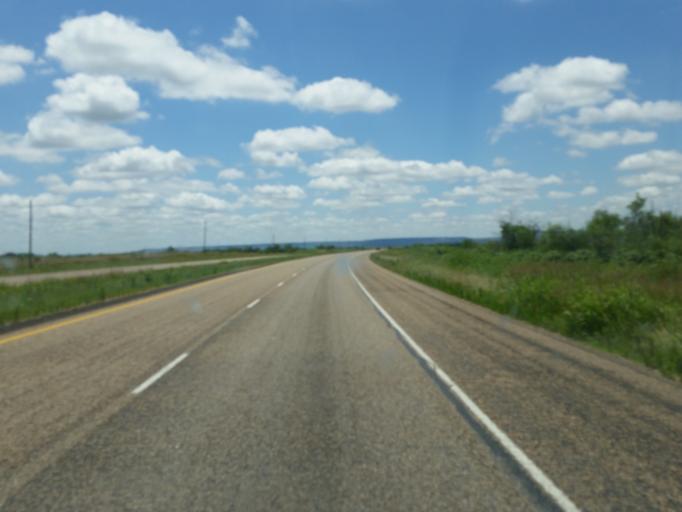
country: US
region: Texas
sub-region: Garza County
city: Post
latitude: 33.0892
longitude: -101.2444
